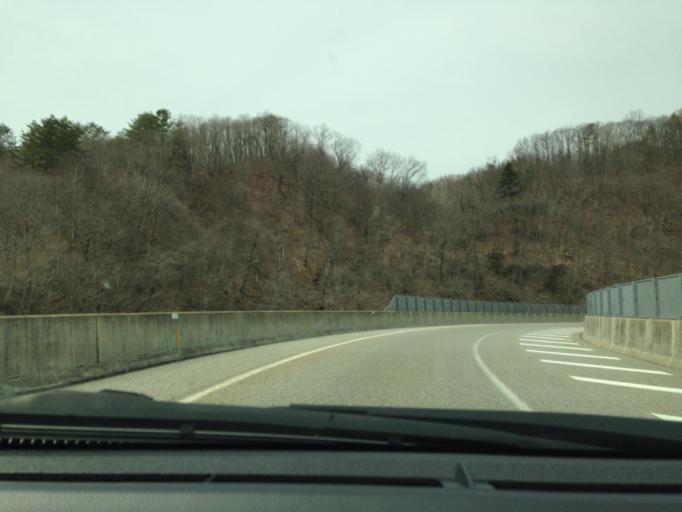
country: JP
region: Gifu
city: Takayama
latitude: 36.1326
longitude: 137.0755
